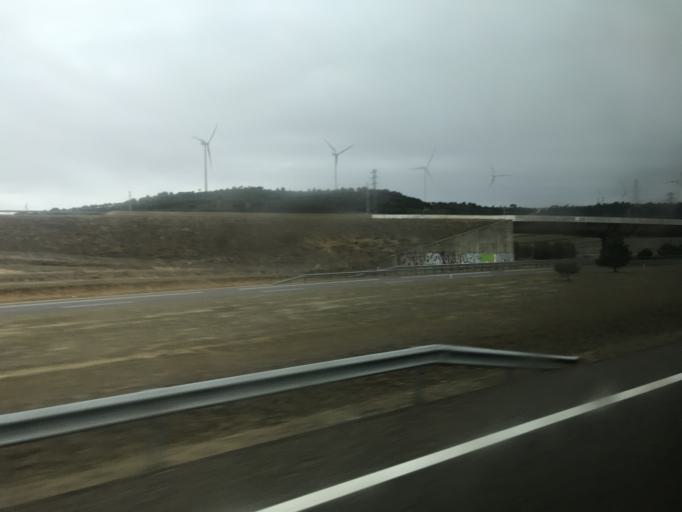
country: ES
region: Castille and Leon
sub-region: Provincia de Palencia
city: Palencia
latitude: 42.0073
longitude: -4.5011
